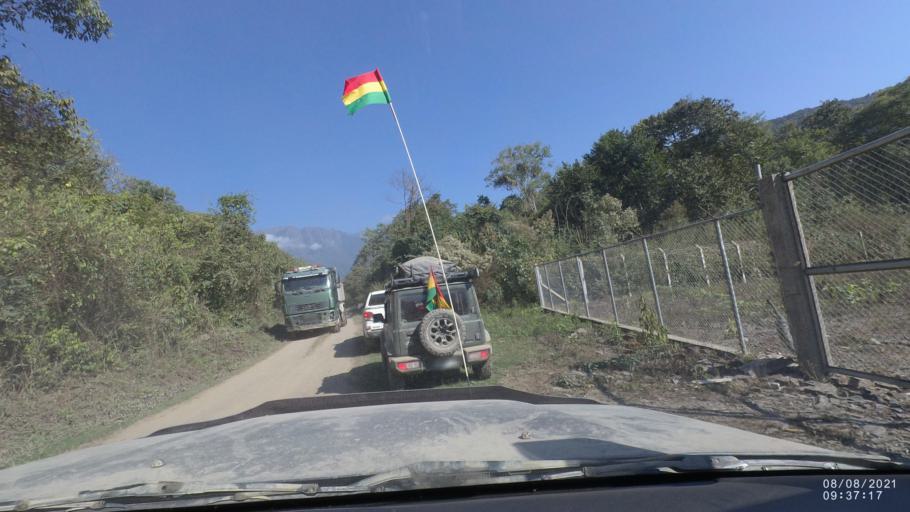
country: BO
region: La Paz
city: Quime
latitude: -16.5945
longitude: -66.7094
